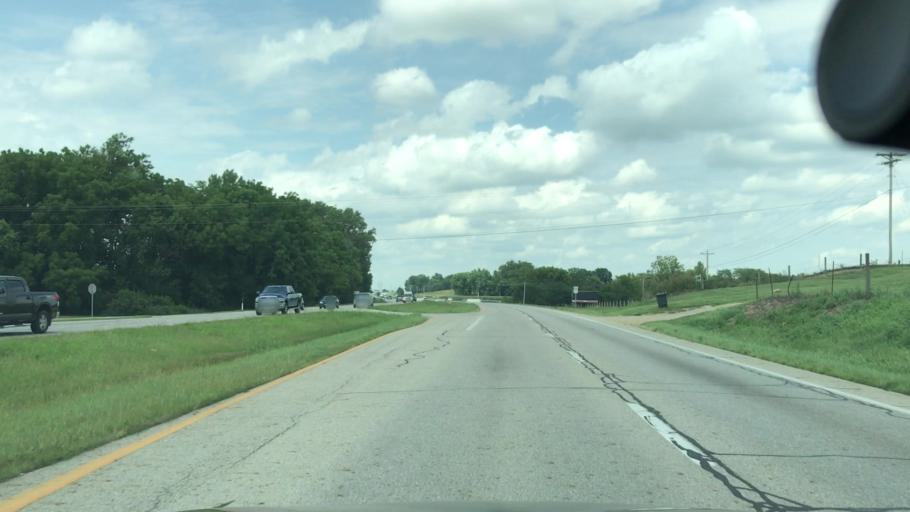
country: US
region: Ohio
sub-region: Pickaway County
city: Logan Elm Village
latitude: 39.5226
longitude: -82.9683
